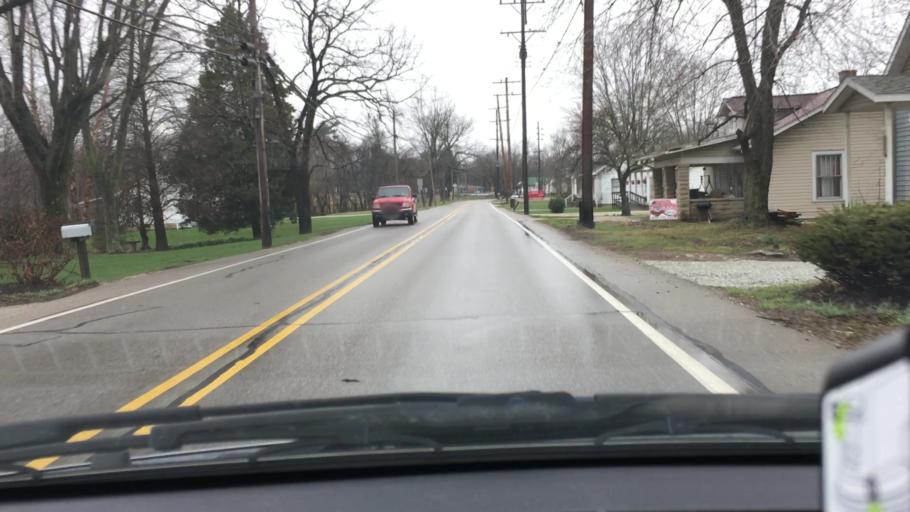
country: US
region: Indiana
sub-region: Lawrence County
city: Bedford
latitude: 38.8747
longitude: -86.4748
